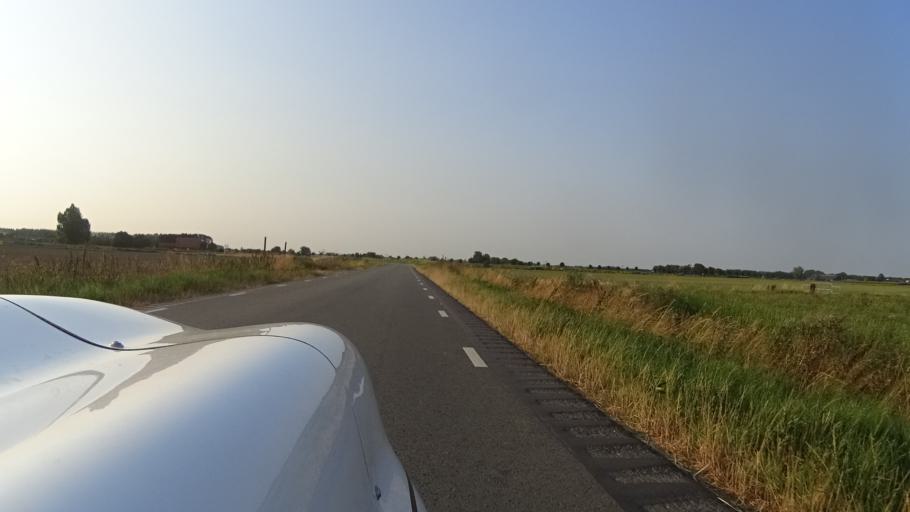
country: NL
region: North Brabant
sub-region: Gemeente Oss
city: Oss
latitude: 51.8514
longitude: 5.5221
